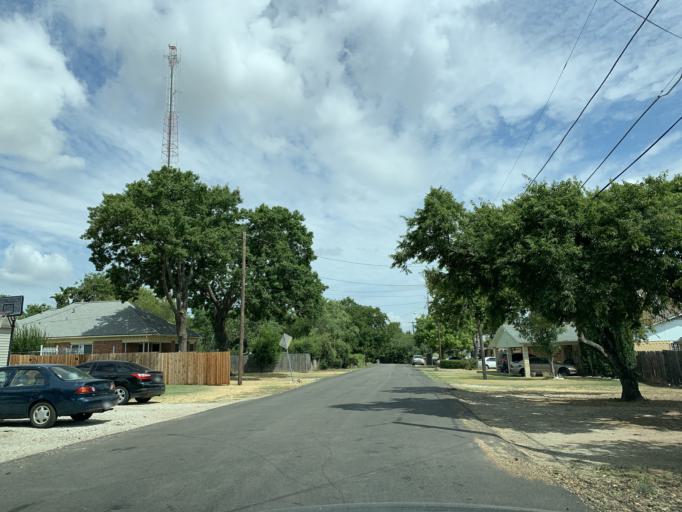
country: US
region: Texas
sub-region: Dallas County
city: Cockrell Hill
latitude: 32.7627
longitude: -96.8676
